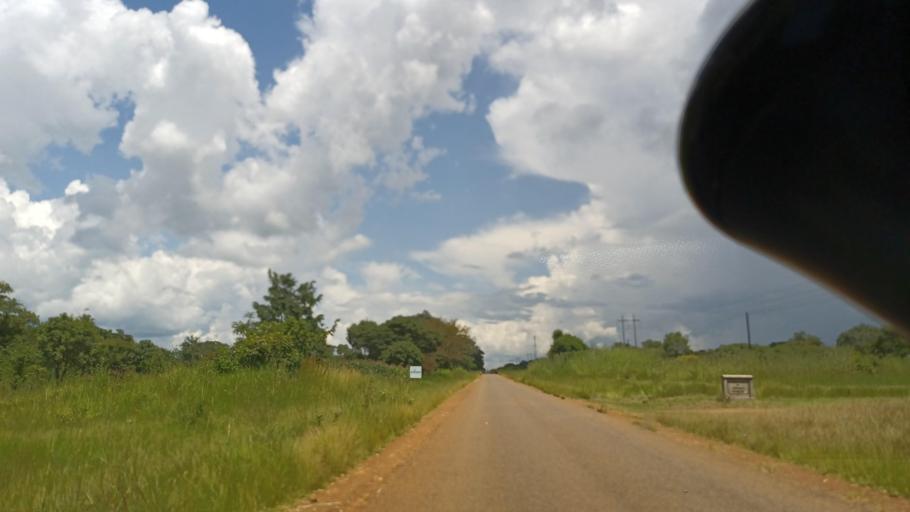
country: ZM
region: North-Western
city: Kasempa
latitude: -12.7873
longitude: 26.0121
